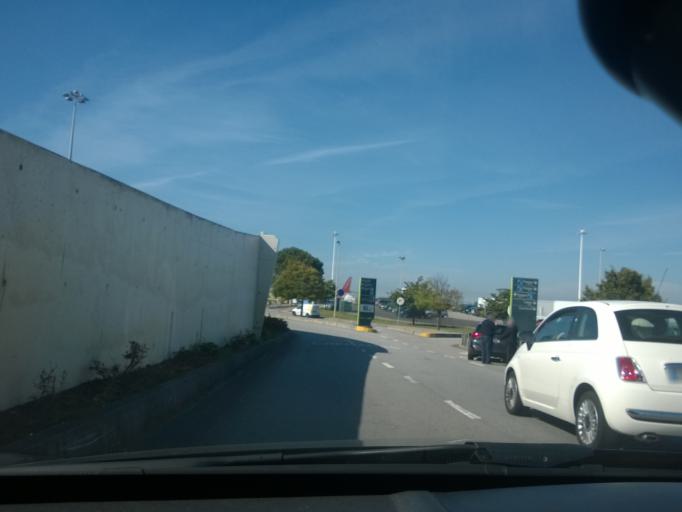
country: PT
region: Porto
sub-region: Matosinhos
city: Santa Cruz do Bispo
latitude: 41.2397
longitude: -8.6706
